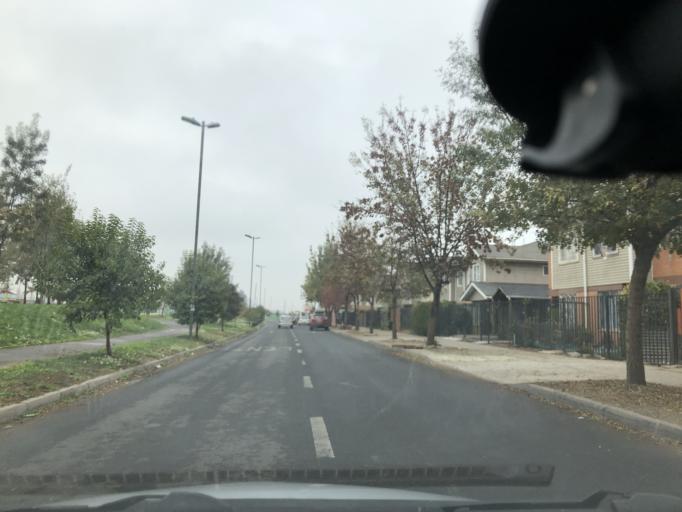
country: CL
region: Santiago Metropolitan
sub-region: Provincia de Cordillera
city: Puente Alto
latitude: -33.5962
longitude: -70.5931
